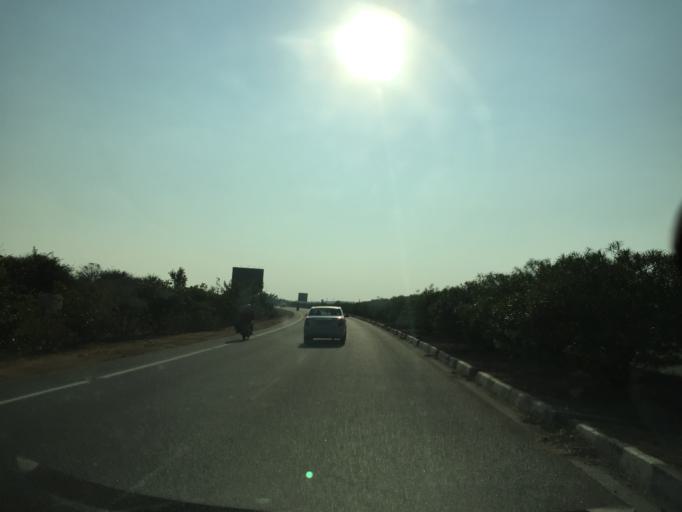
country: IN
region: Telangana
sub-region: Nalgonda
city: Bhongir
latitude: 17.5120
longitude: 78.9013
